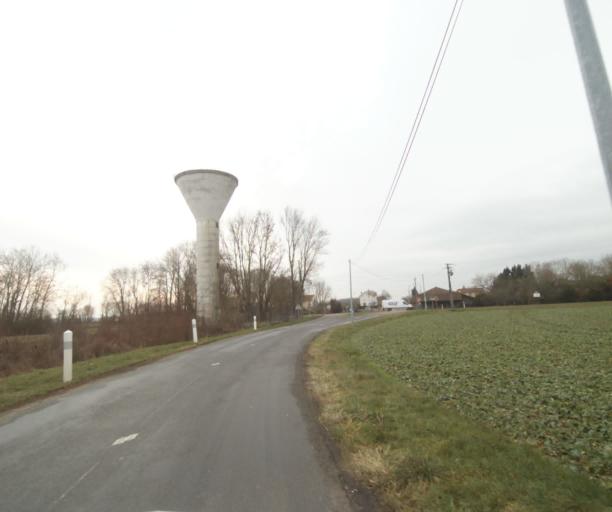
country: FR
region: Champagne-Ardenne
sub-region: Departement de la Haute-Marne
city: Villiers-en-Lieu
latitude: 48.6478
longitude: 4.8744
